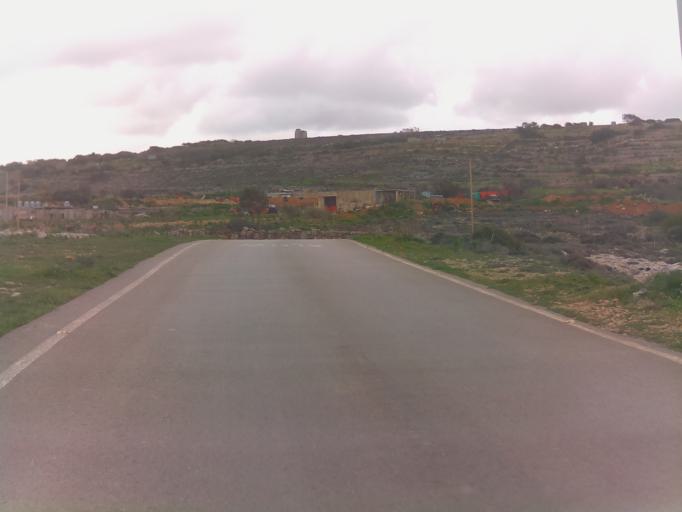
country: MT
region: Il-Mellieha
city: Mellieha
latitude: 35.9804
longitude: 14.3337
